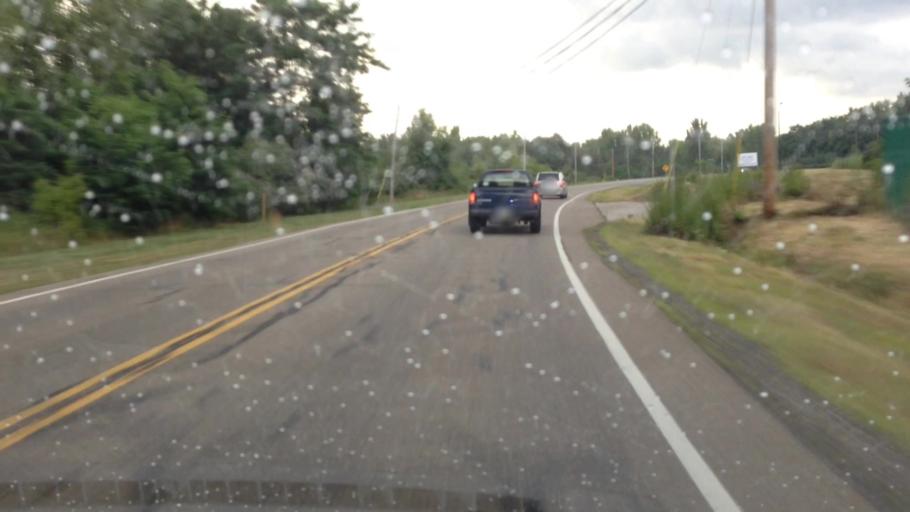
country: US
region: Ohio
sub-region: Summit County
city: Portage Lakes
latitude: 41.0156
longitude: -81.5329
